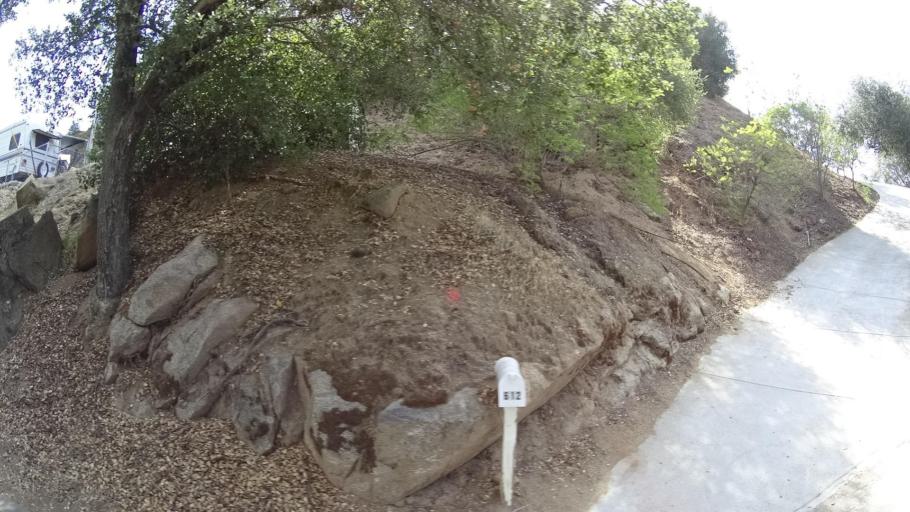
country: US
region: California
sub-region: San Diego County
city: Harbison Canyon
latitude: 32.8175
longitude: -116.8317
